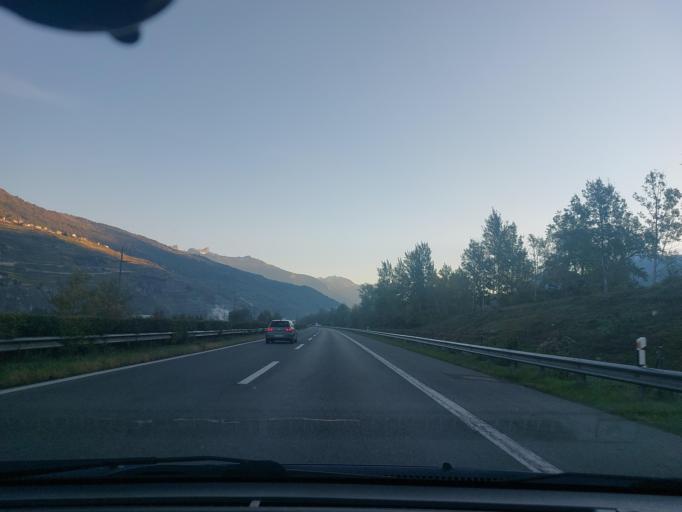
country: CH
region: Valais
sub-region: Sierre District
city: Grone
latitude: 46.2519
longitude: 7.4364
